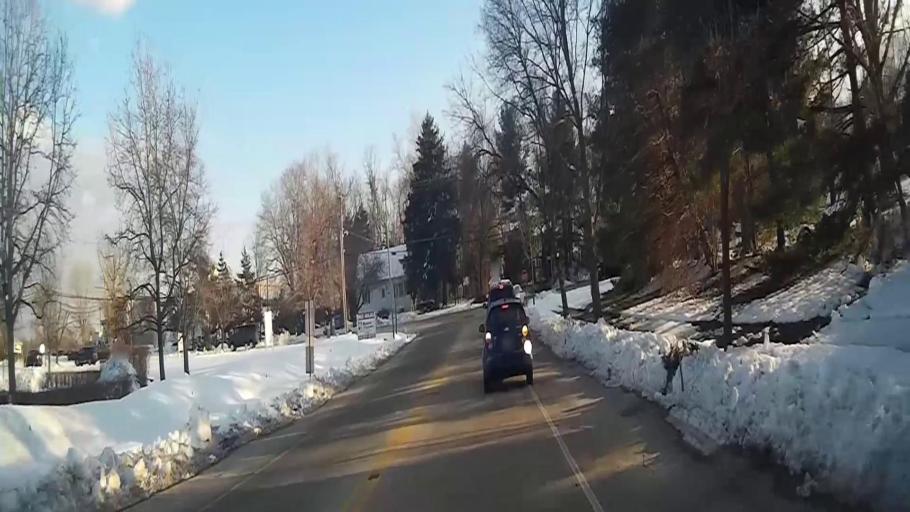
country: US
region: New Jersey
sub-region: Burlington County
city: Marlton
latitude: 39.8809
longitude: -74.9253
